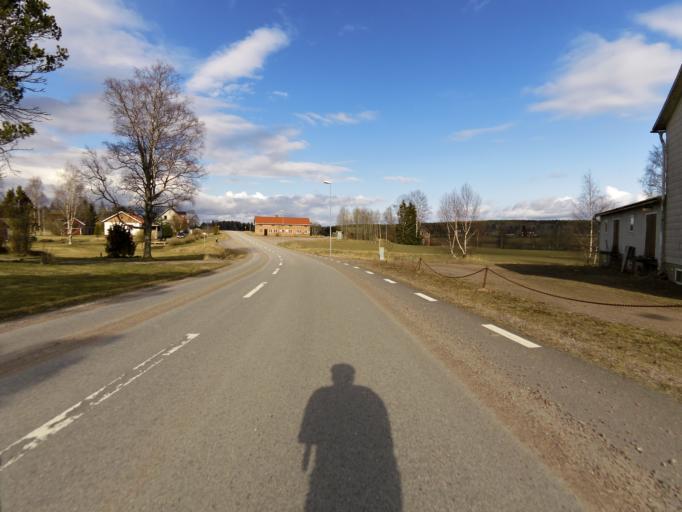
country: SE
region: Dalarna
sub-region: Avesta Kommun
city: Horndal
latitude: 60.4522
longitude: 16.4520
